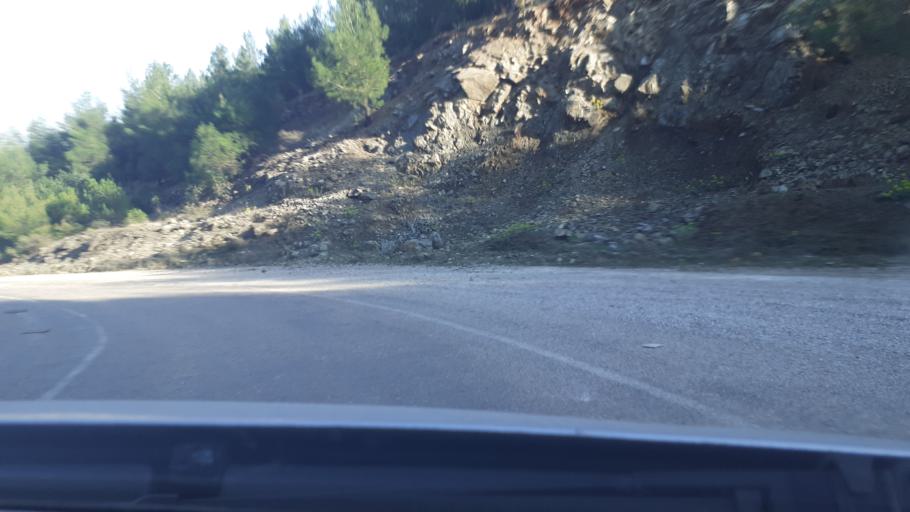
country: TR
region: Hatay
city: Aktepe
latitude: 36.7346
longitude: 36.4656
